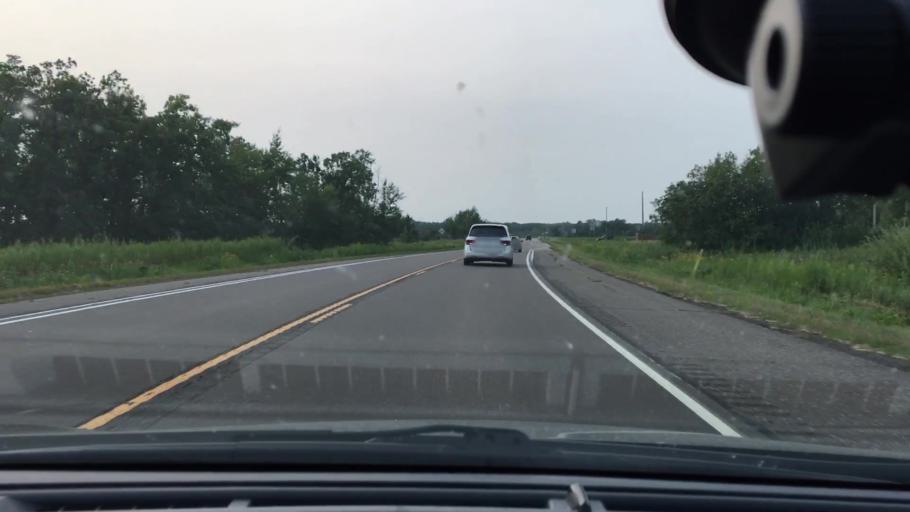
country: US
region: Minnesota
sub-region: Mille Lacs County
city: Vineland
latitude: 46.1564
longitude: -93.7554
